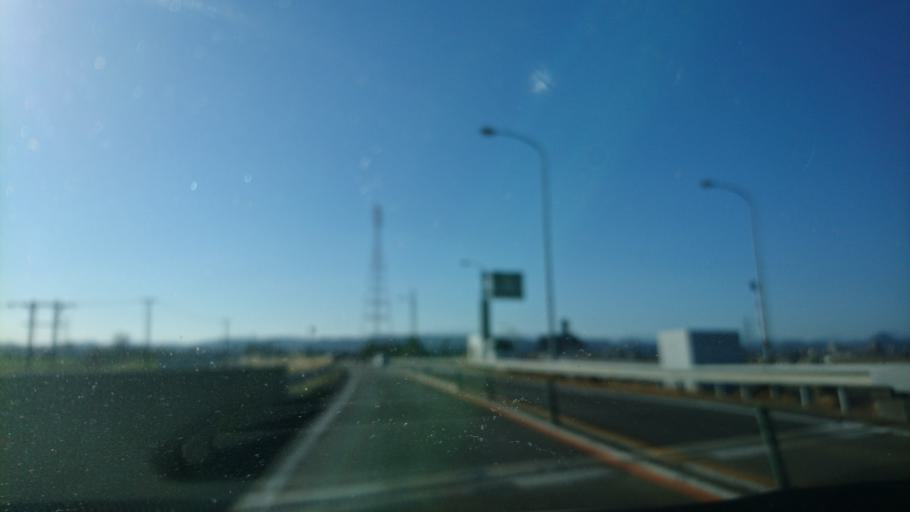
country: JP
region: Miyagi
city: Sendai
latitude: 38.2124
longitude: 140.9019
